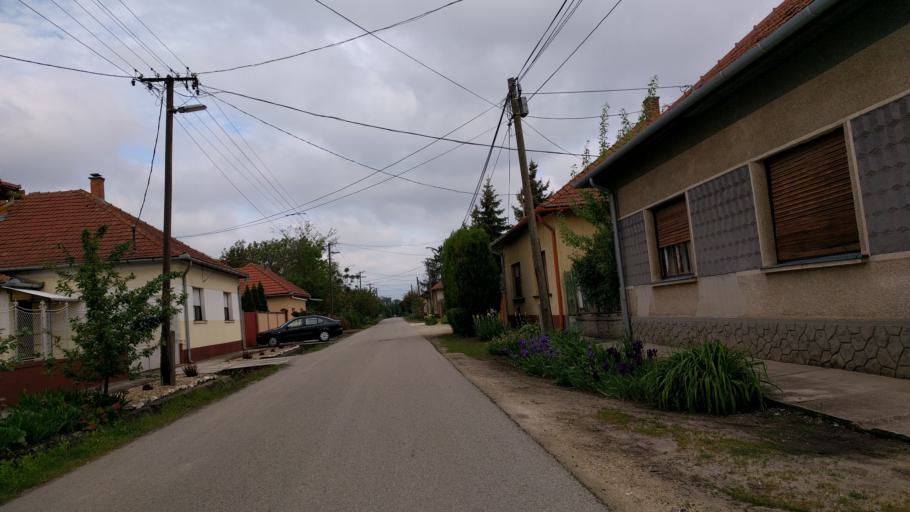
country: HU
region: Bacs-Kiskun
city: Tiszakecske
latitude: 46.9321
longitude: 20.1008
